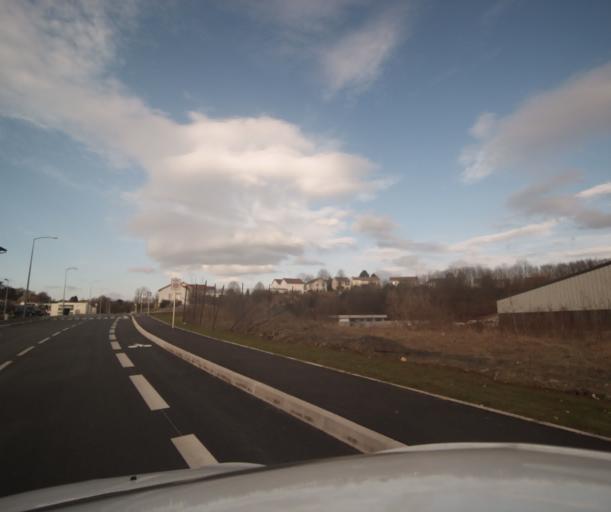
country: FR
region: Franche-Comte
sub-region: Departement du Doubs
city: Besancon
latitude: 47.2657
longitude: 6.0273
